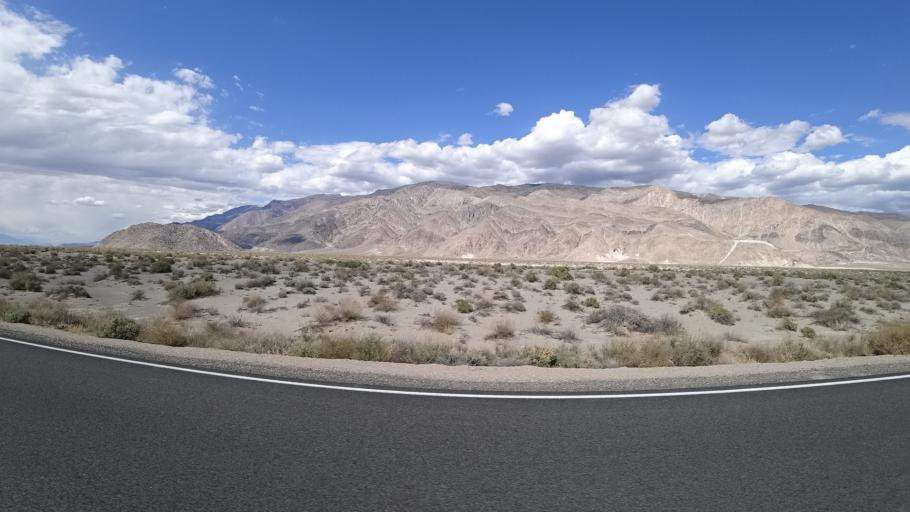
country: US
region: California
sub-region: Inyo County
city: Lone Pine
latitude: 36.5680
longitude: -117.9833
